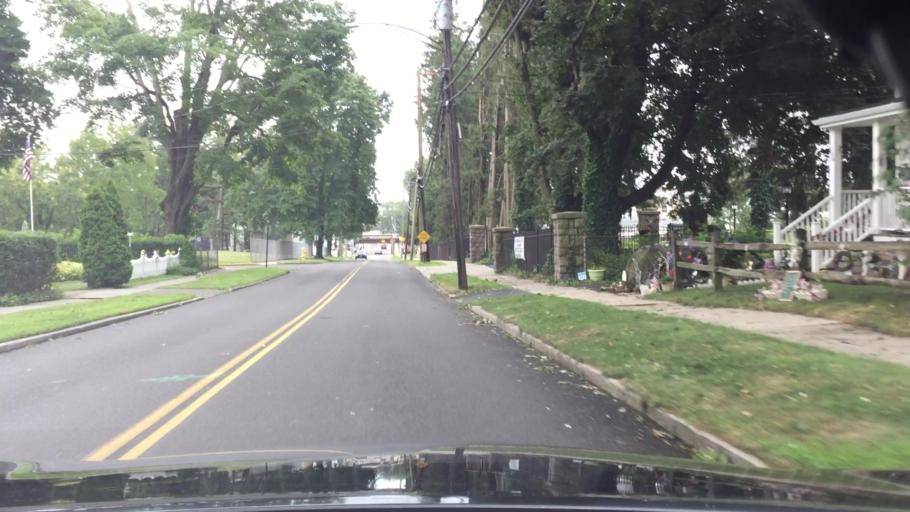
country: US
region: Connecticut
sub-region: New Haven County
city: City of Milford (balance)
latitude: 41.2244
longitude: -73.0621
